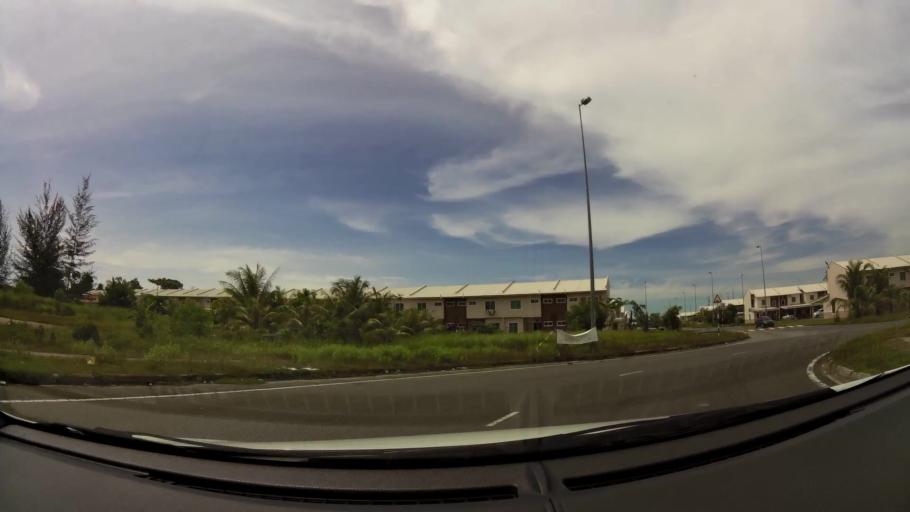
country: BN
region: Belait
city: Kuala Belait
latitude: 4.5941
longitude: 114.2780
